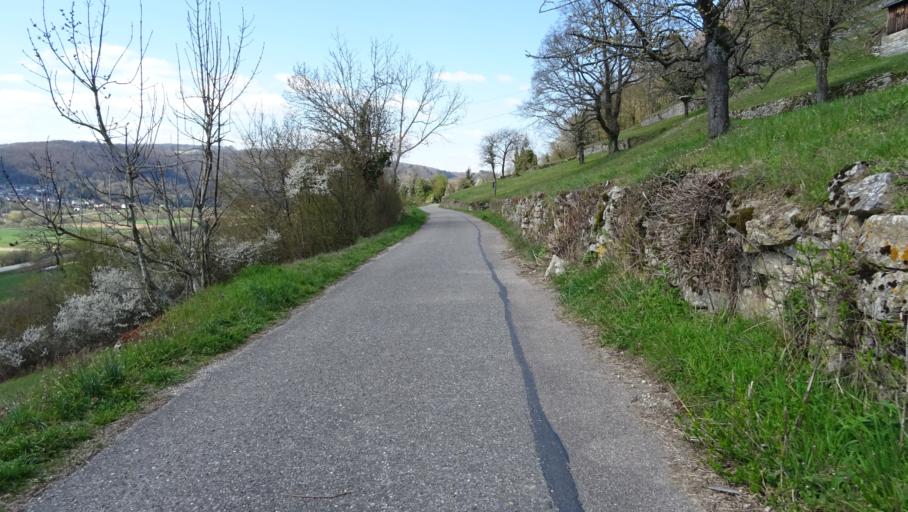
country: DE
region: Baden-Wuerttemberg
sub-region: Karlsruhe Region
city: Neckarzimmern
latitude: 49.3245
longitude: 9.1227
